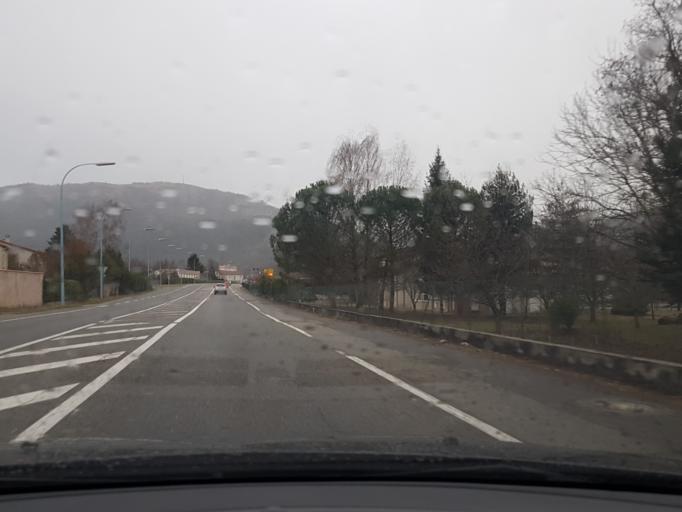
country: FR
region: Midi-Pyrenees
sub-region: Departement de l'Ariege
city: Foix
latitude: 42.9933
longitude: 1.6156
